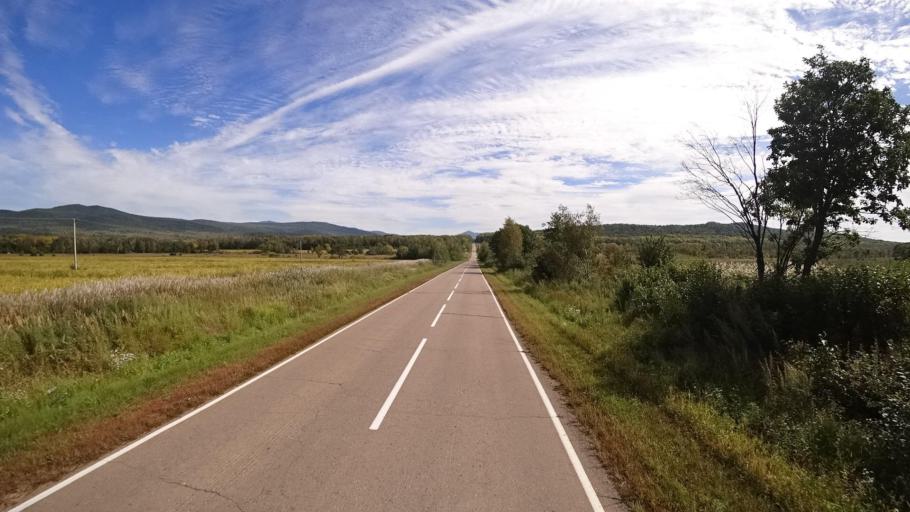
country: RU
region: Primorskiy
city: Yakovlevka
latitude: 44.4124
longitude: 133.5867
